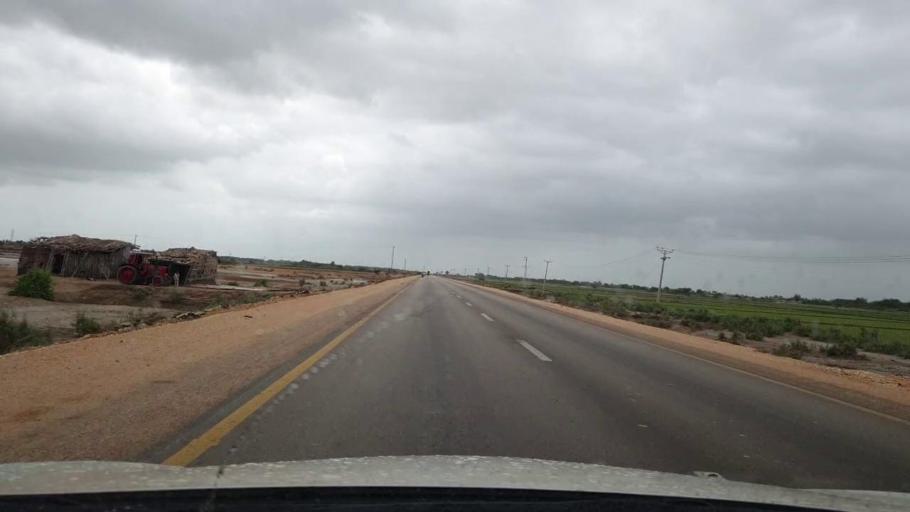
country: PK
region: Sindh
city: Badin
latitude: 24.6559
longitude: 68.7087
